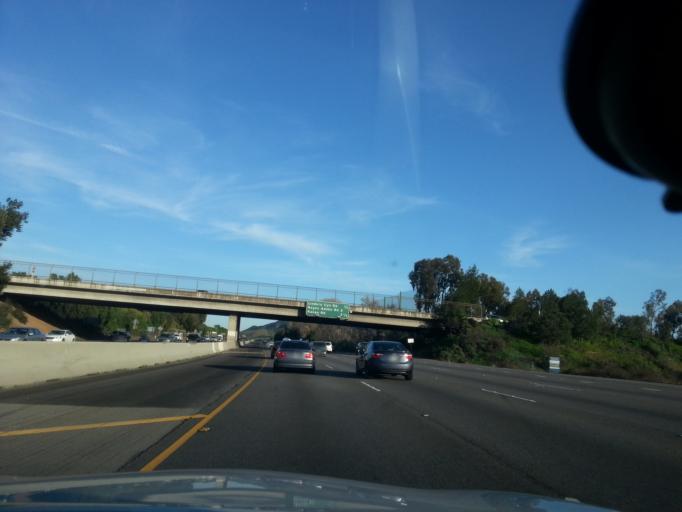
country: US
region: California
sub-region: Los Angeles County
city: Westlake Village
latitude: 34.1535
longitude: -118.8186
